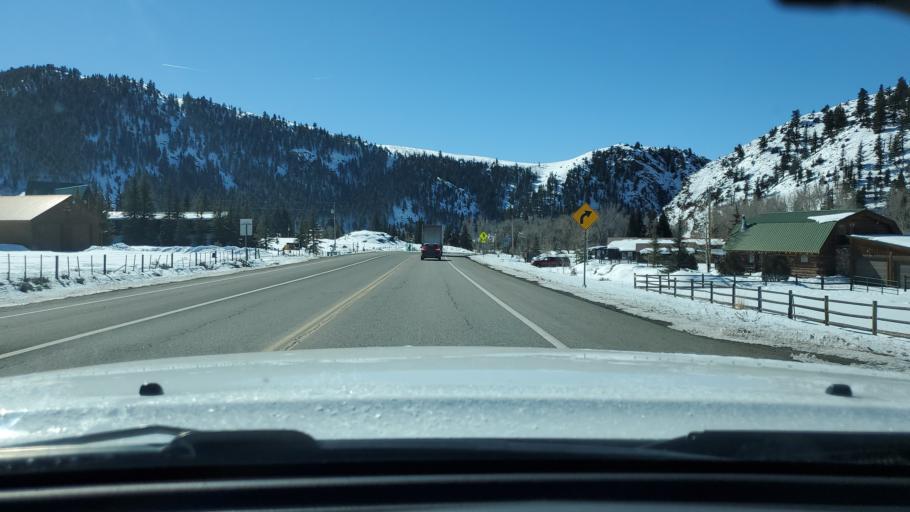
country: US
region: Colorado
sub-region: Gunnison County
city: Gunnison
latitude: 38.6670
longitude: -106.8458
